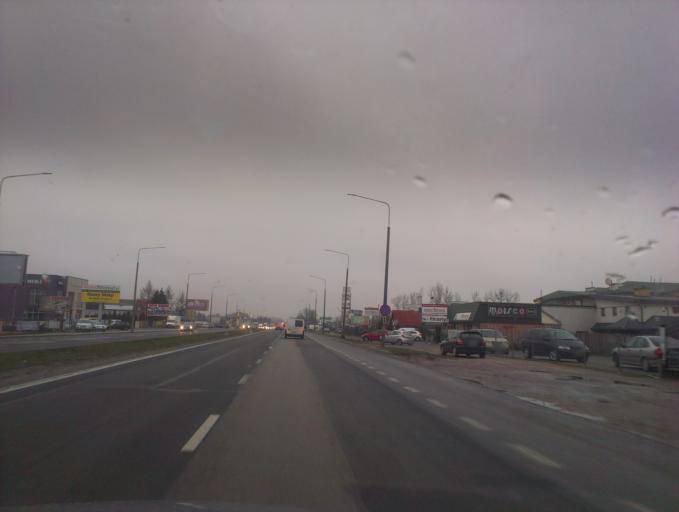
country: PL
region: Masovian Voivodeship
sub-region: Radom
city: Radom
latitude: 51.4356
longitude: 21.1476
